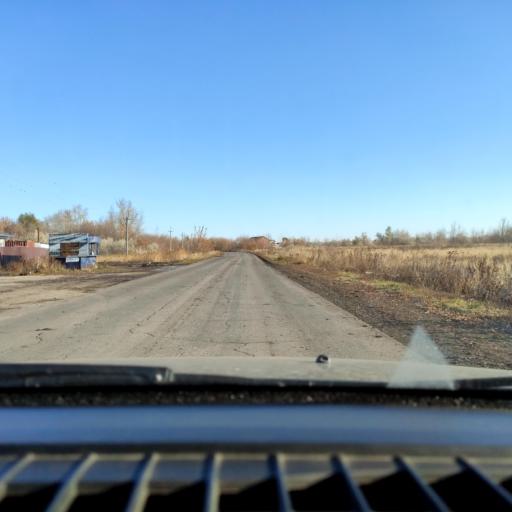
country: RU
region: Samara
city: Tol'yatti
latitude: 53.6384
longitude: 49.3119
